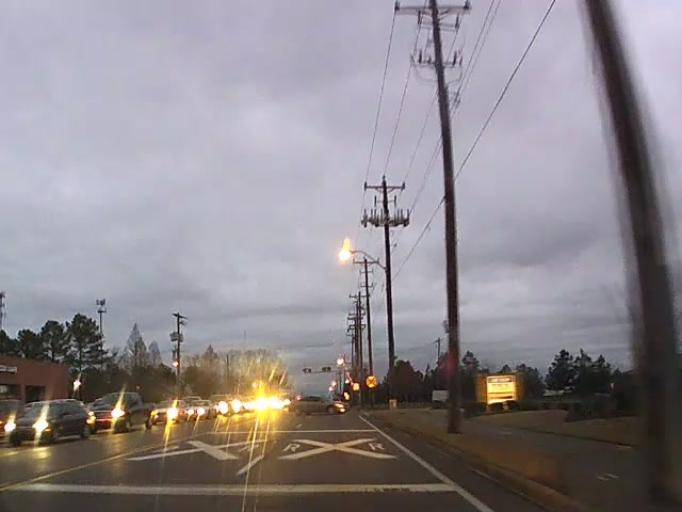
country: US
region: Tennessee
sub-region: Shelby County
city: Collierville
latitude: 35.0451
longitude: -89.6892
